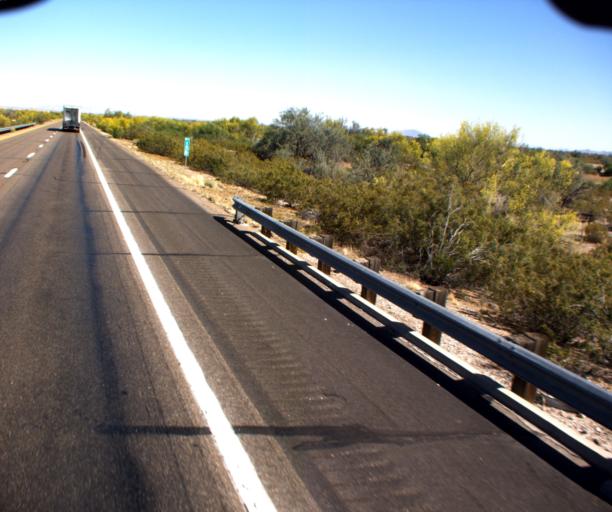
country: US
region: Arizona
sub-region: Pinal County
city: Maricopa
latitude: 32.8301
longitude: -112.0254
